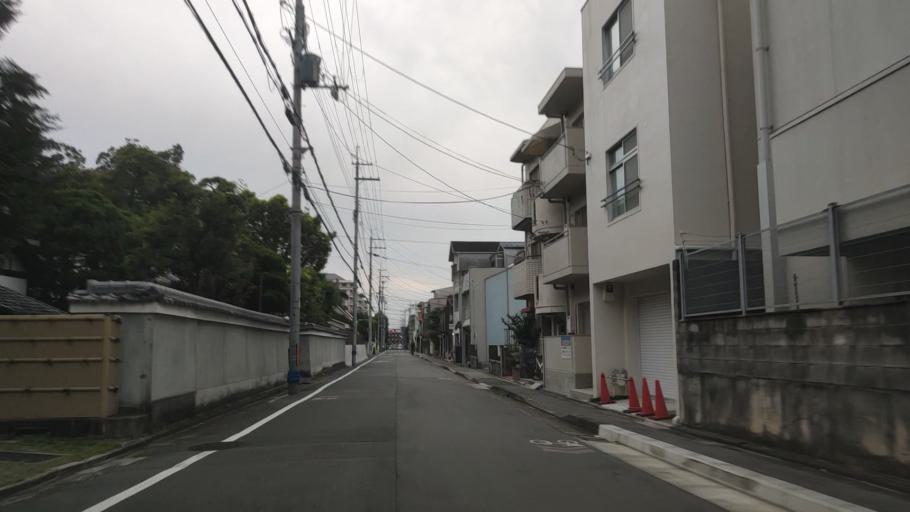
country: JP
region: Kyoto
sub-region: Kyoto-shi
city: Kamigyo-ku
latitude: 35.0235
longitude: 135.7760
